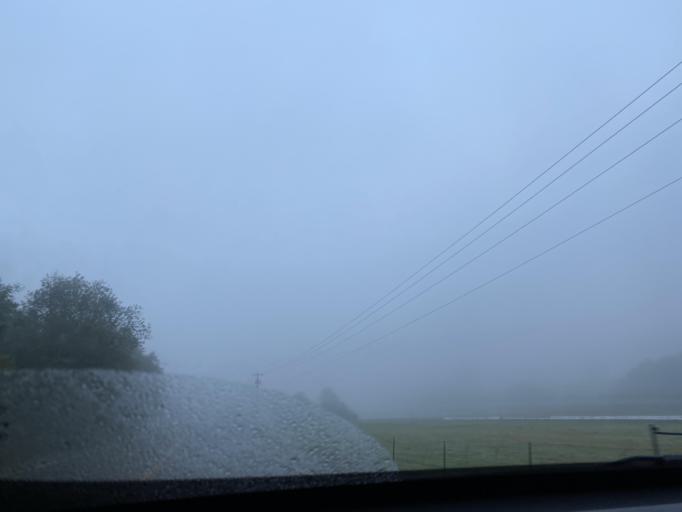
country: US
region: Washington
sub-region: Clallam County
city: Forks
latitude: 47.9361
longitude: -124.3971
